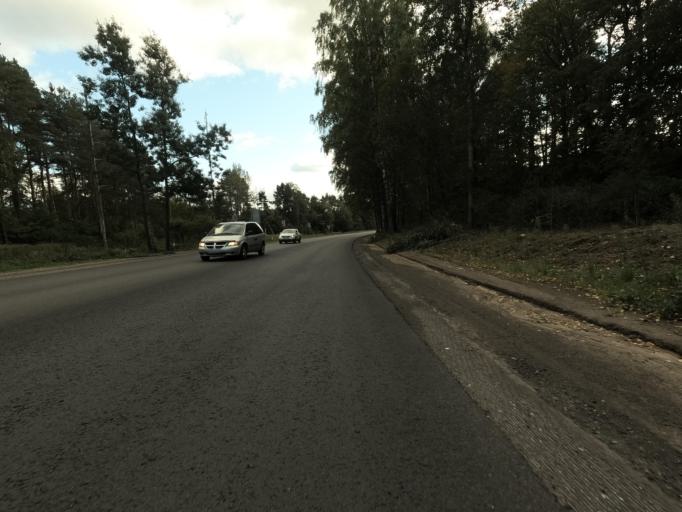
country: RU
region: Leningrad
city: Koltushi
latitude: 59.9476
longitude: 30.6578
